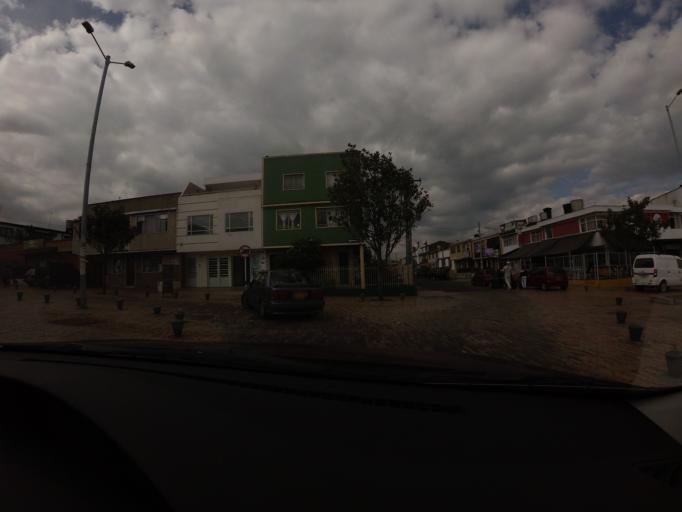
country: CO
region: Cundinamarca
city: Zipaquira
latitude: 5.0222
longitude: -74.0013
